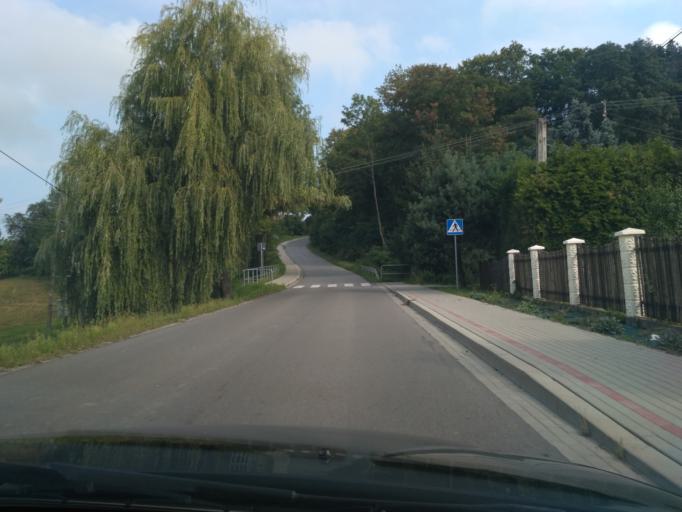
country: PL
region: Subcarpathian Voivodeship
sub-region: Powiat strzyzowski
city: Czudec
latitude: 49.9563
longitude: 21.8460
